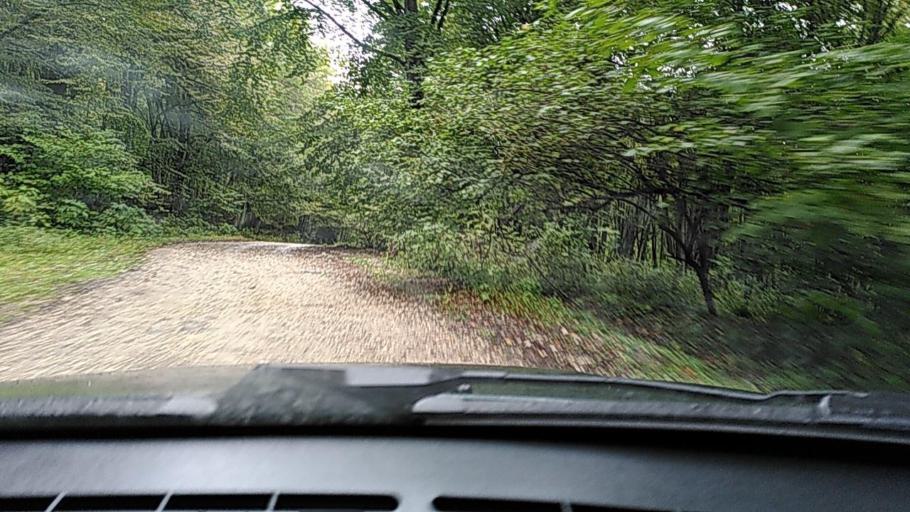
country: RU
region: Kabardino-Balkariya
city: Belaya Rechka
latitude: 43.4069
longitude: 43.4668
